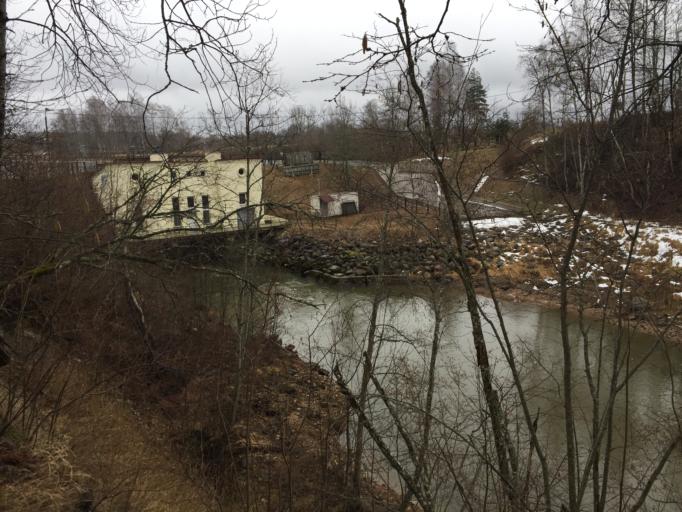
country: LV
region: Saldus Rajons
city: Saldus
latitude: 56.6975
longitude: 22.2949
